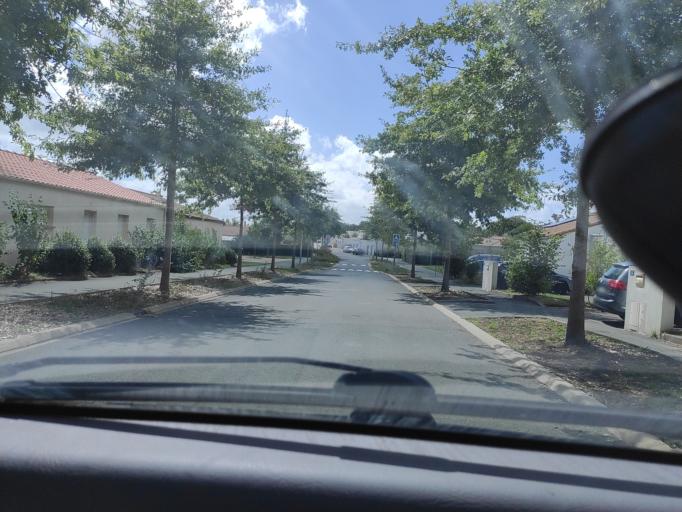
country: FR
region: Pays de la Loire
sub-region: Departement de la Vendee
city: Mouilleron-le-Captif
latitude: 46.6906
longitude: -1.4510
